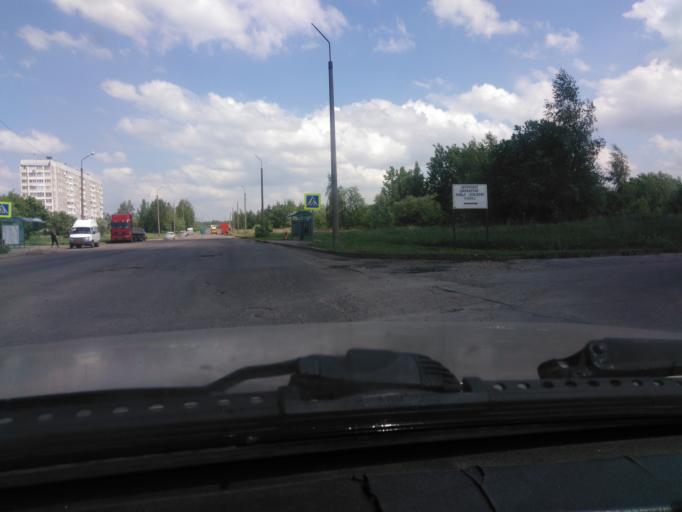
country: BY
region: Mogilev
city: Mahilyow
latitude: 53.9457
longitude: 30.3708
